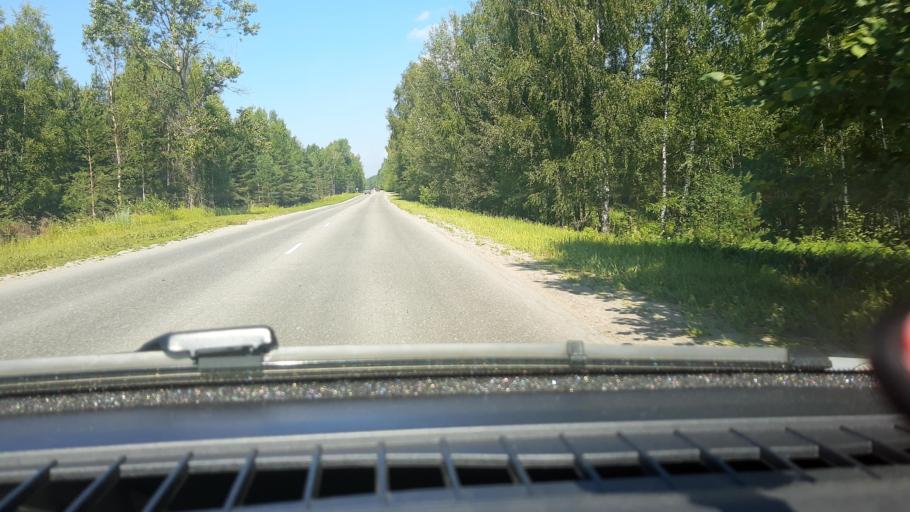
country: RU
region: Nizjnij Novgorod
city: Afonino
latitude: 56.3087
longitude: 44.1743
